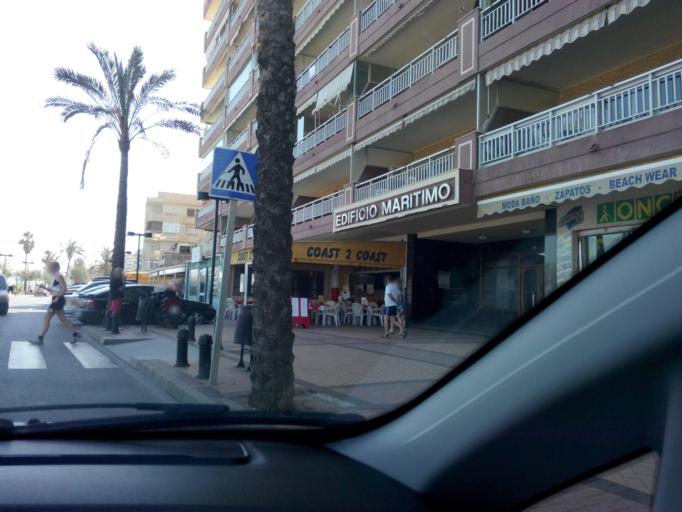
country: ES
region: Andalusia
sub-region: Provincia de Malaga
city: Fuengirola
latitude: 36.5626
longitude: -4.6050
